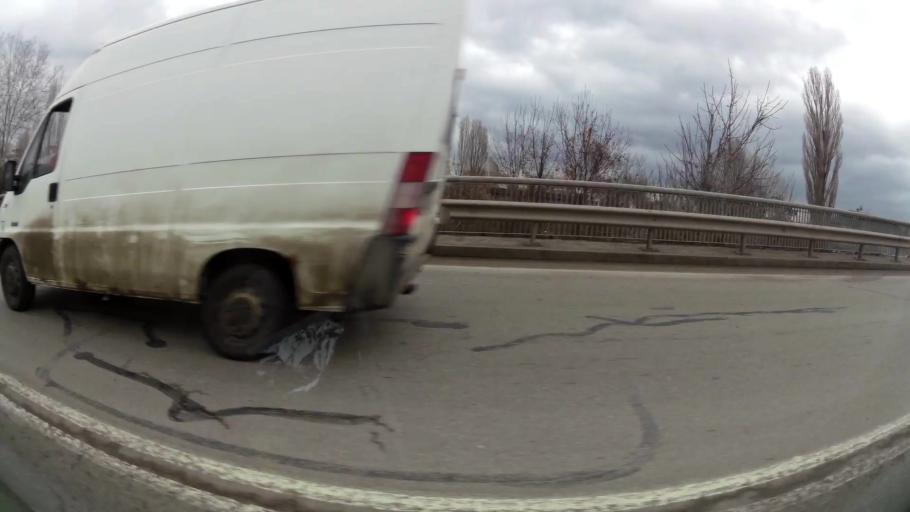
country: BG
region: Sofia-Capital
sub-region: Stolichna Obshtina
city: Sofia
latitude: 42.7300
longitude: 23.2831
